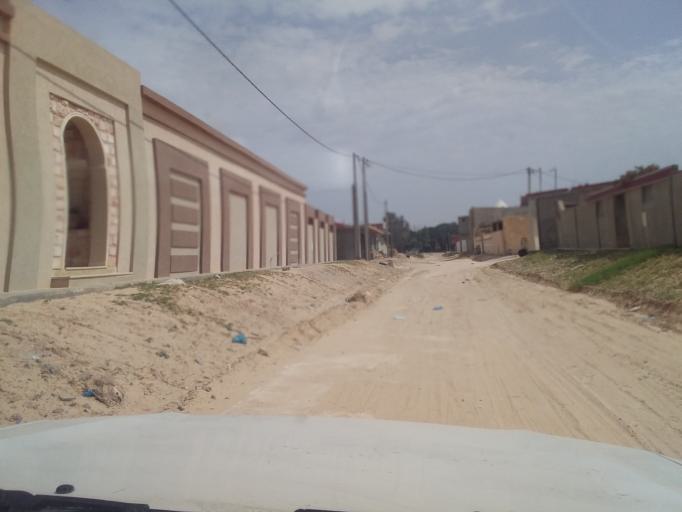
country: TN
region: Qabis
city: Matmata
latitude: 33.6218
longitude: 10.2722
